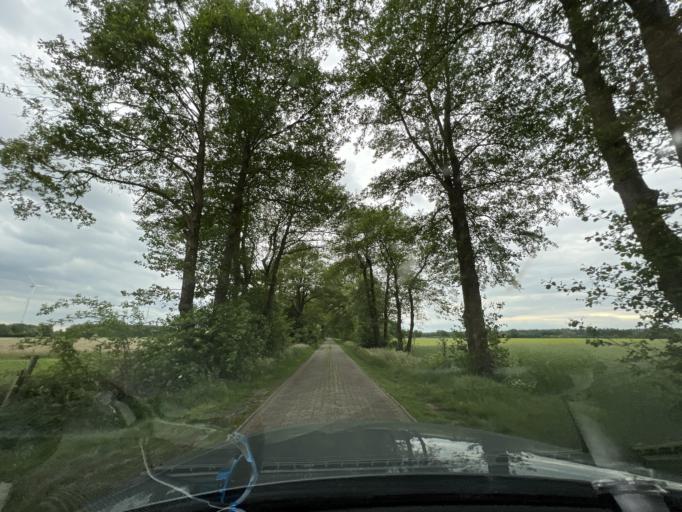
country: DE
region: Lower Saxony
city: Hatten
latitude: 53.0458
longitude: 8.3147
